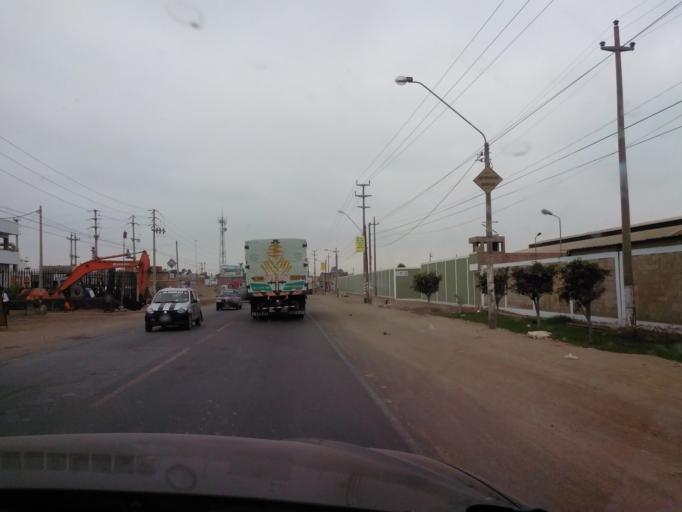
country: PE
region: Ica
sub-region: Provincia de Chincha
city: Chincha Baja
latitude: -13.4494
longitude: -76.1360
